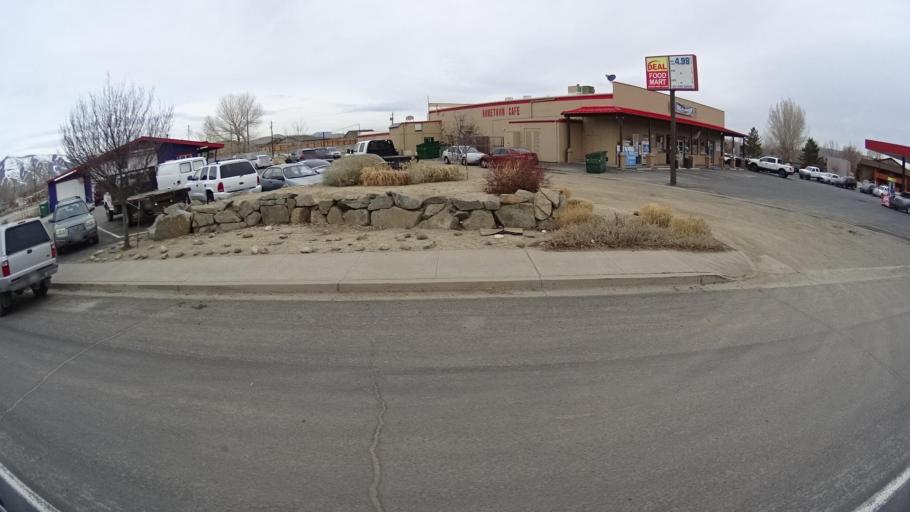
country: US
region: Nevada
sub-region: Washoe County
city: Lemmon Valley
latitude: 39.6379
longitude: -119.8428
